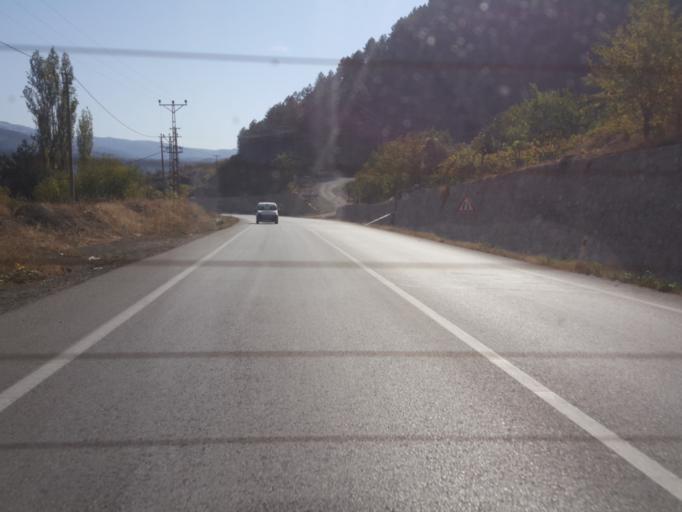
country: TR
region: Corum
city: Iskilip
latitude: 40.7377
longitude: 34.4520
